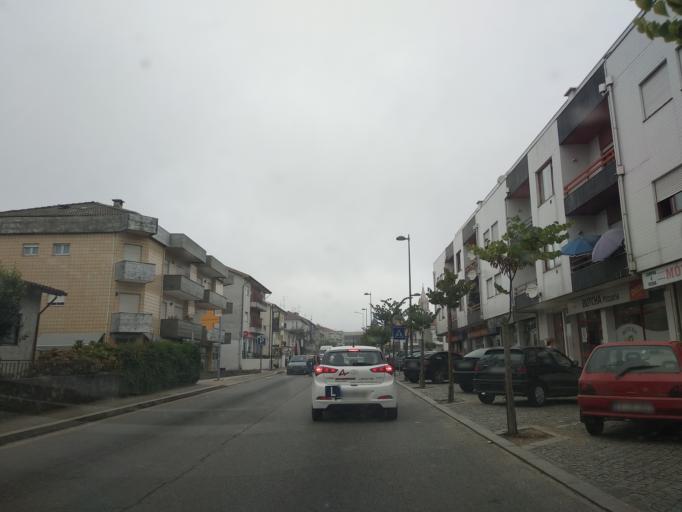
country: PT
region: Braga
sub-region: Vila Verde
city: Vila Verde
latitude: 41.6453
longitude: -8.4357
